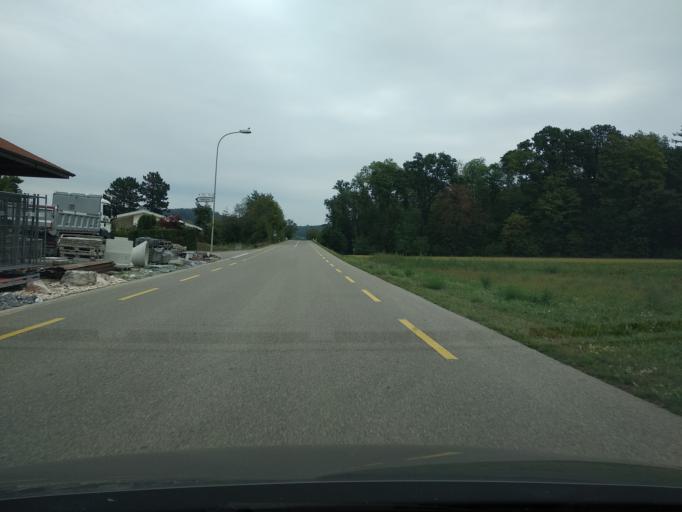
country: CH
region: Zurich
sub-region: Bezirk Andelfingen
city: Marthalen
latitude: 47.6342
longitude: 8.6602
